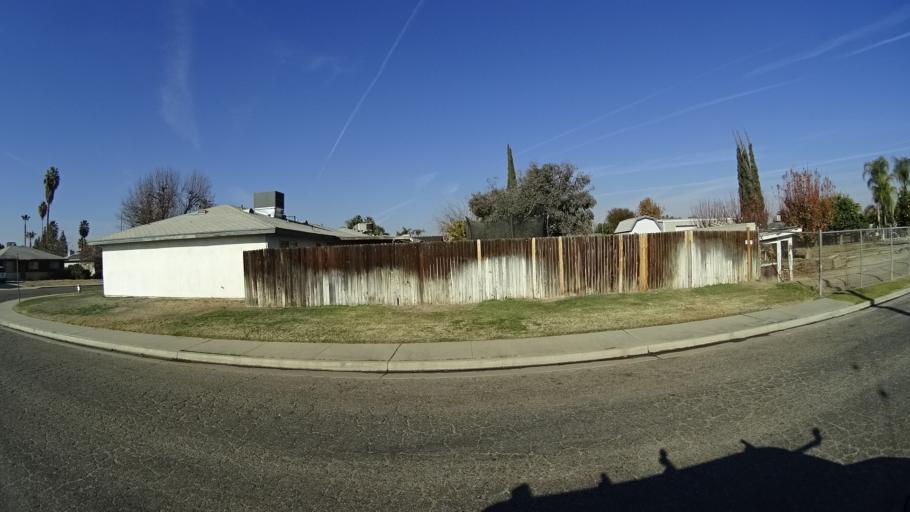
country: US
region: California
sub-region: Kern County
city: Greenfield
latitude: 35.3003
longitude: -119.0506
